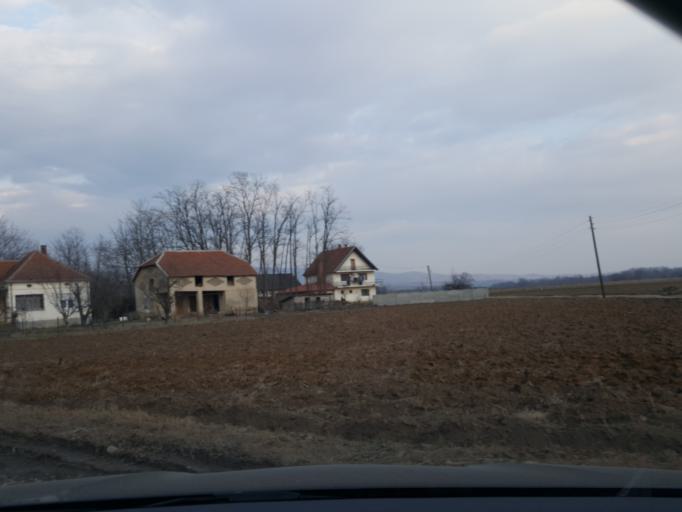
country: RS
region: Central Serbia
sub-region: Nisavski Okrug
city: Aleksinac
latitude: 43.5880
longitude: 21.6141
